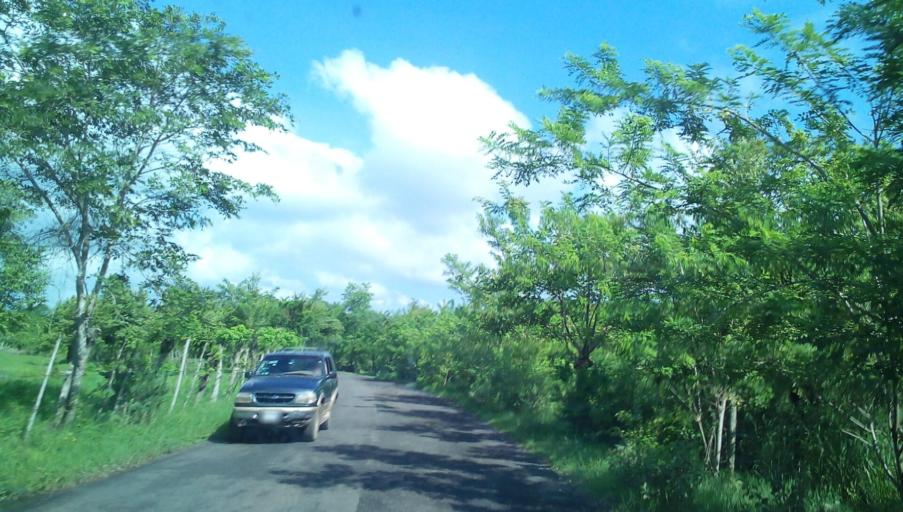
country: MX
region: Veracruz
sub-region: Citlaltepetl
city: Las Sabinas
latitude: 21.3457
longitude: -97.8912
